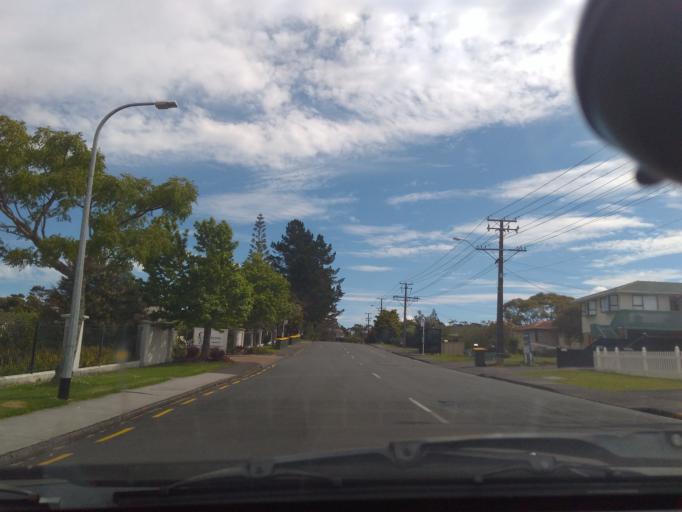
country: NZ
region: Auckland
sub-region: Auckland
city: Titirangi
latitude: -36.9354
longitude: 174.6716
